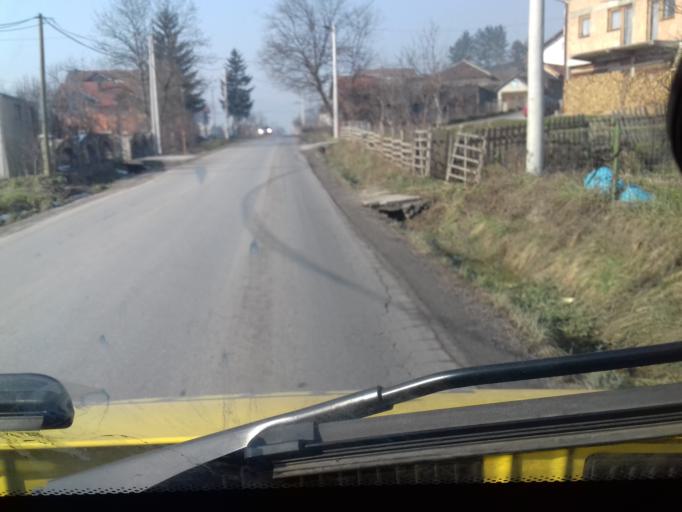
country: BA
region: Federation of Bosnia and Herzegovina
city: Ilijas
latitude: 43.9413
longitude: 18.2774
